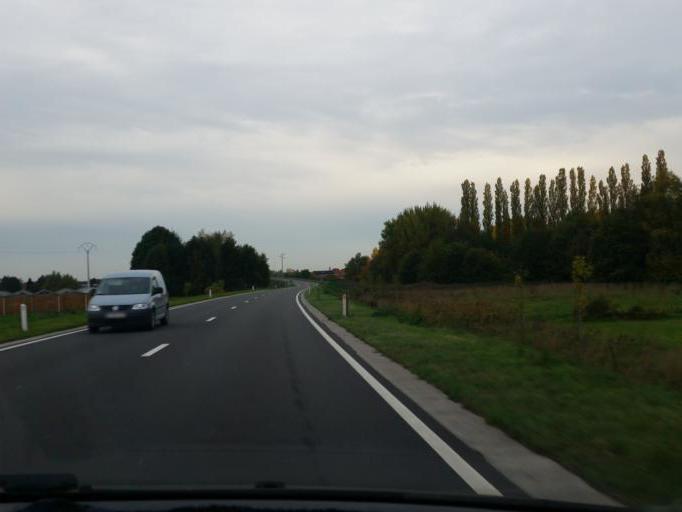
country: BE
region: Flanders
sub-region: Provincie Antwerpen
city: Sint-Katelijne-Waver
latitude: 51.0492
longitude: 4.5251
